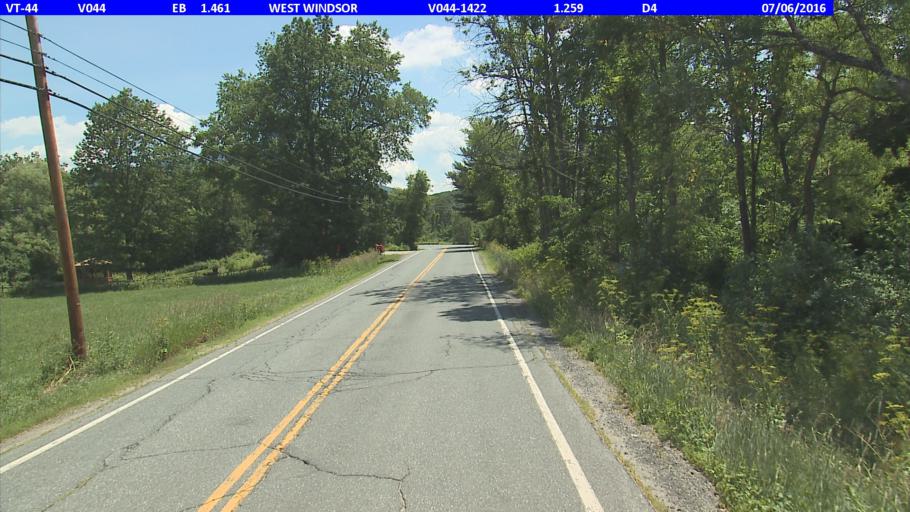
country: US
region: Vermont
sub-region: Windsor County
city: Windsor
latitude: 43.4563
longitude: -72.5169
